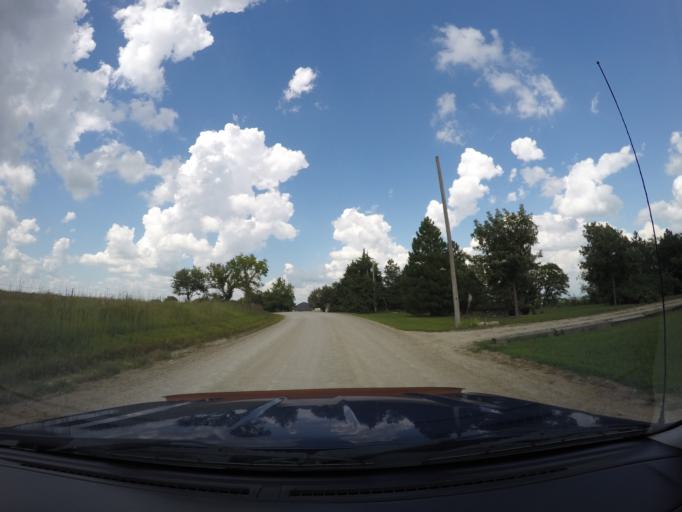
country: US
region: Kansas
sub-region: Wabaunsee County
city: Alma
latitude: 39.0234
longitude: -96.2935
